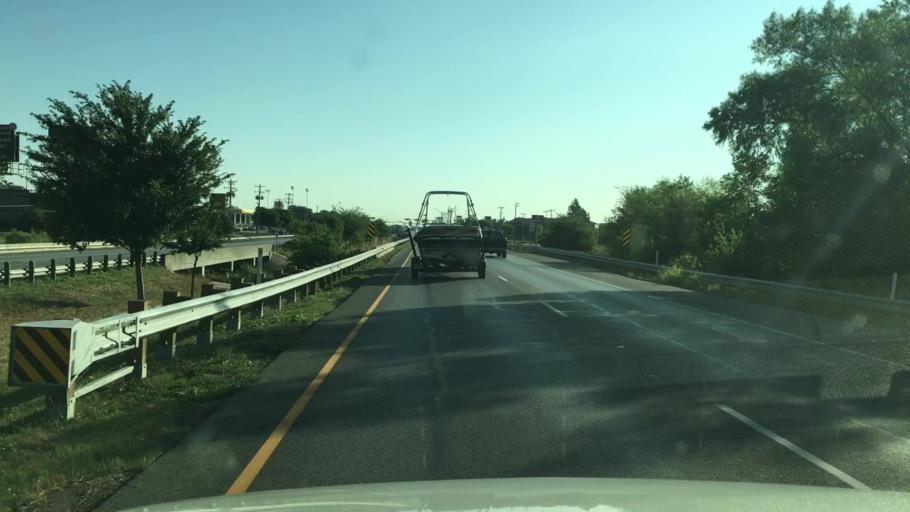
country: US
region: Texas
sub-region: Johnson County
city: Burleson
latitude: 32.5225
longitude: -97.3464
